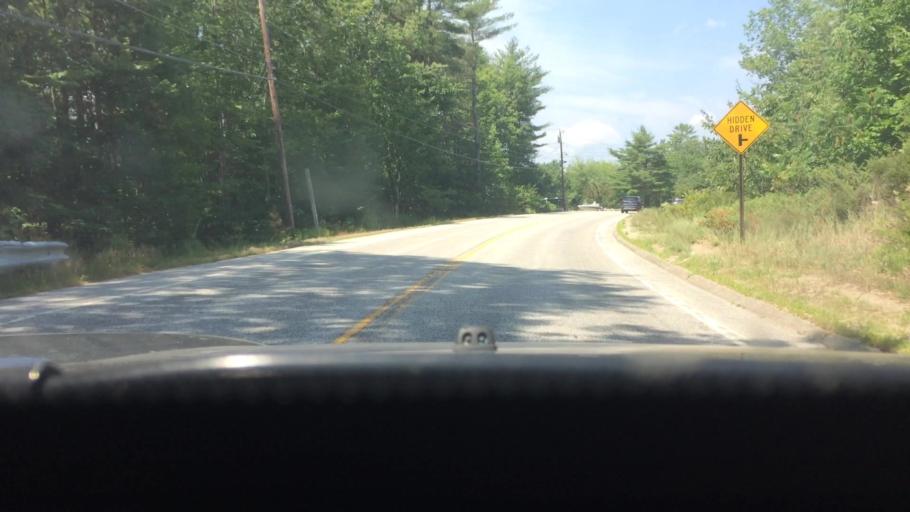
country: US
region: Maine
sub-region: Androscoggin County
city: Mechanic Falls
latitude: 44.1109
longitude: -70.4193
